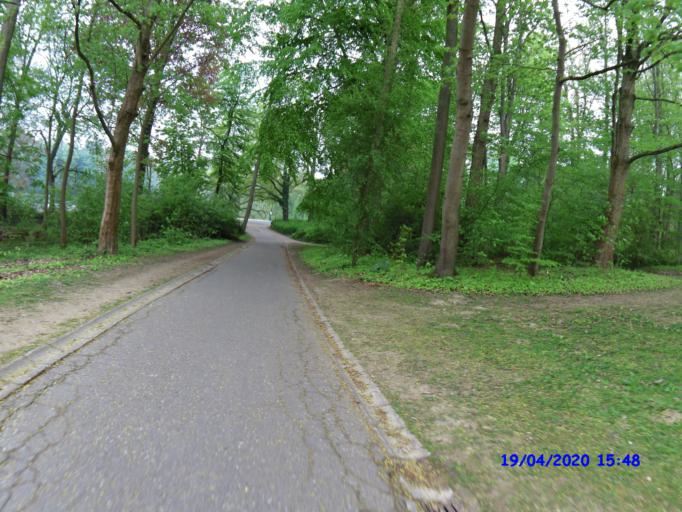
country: BE
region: Flanders
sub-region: Provincie Vlaams-Brabant
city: Kraainem
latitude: 50.8319
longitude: 4.4307
